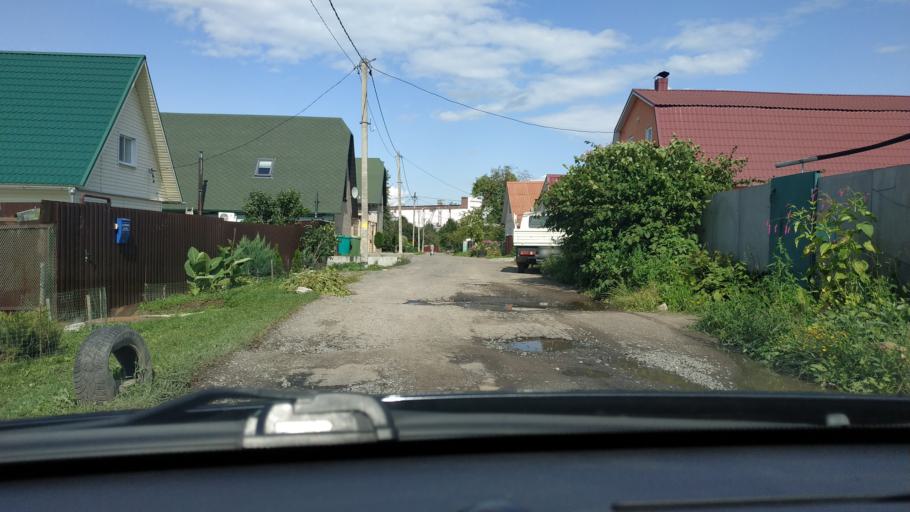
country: BY
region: Mogilev
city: Buynichy
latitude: 53.9017
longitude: 30.2917
